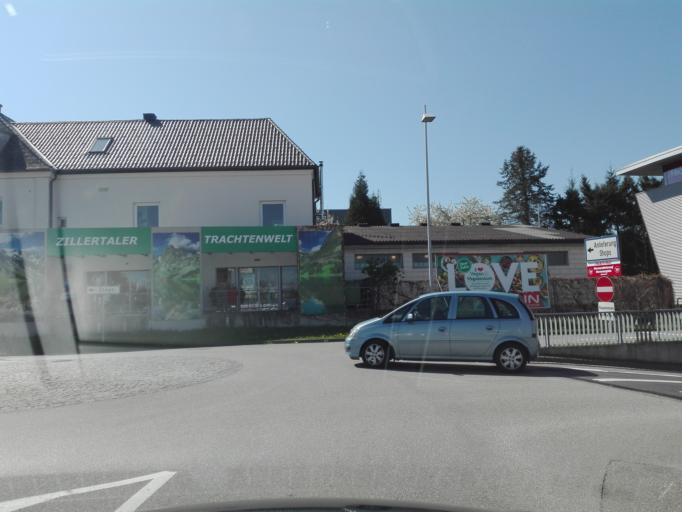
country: AT
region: Upper Austria
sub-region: Steyr Stadt
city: Steyr
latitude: 48.0533
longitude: 14.4201
